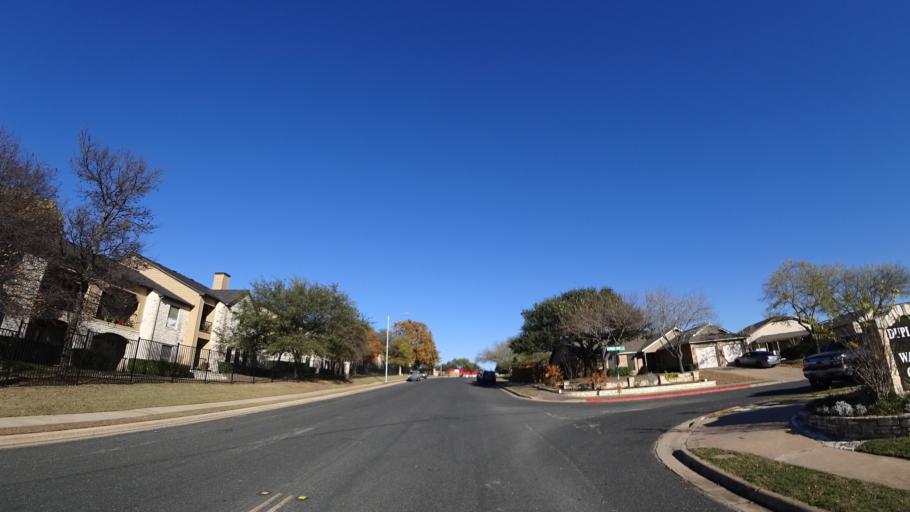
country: US
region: Texas
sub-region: Travis County
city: Wells Branch
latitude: 30.4083
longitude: -97.6954
